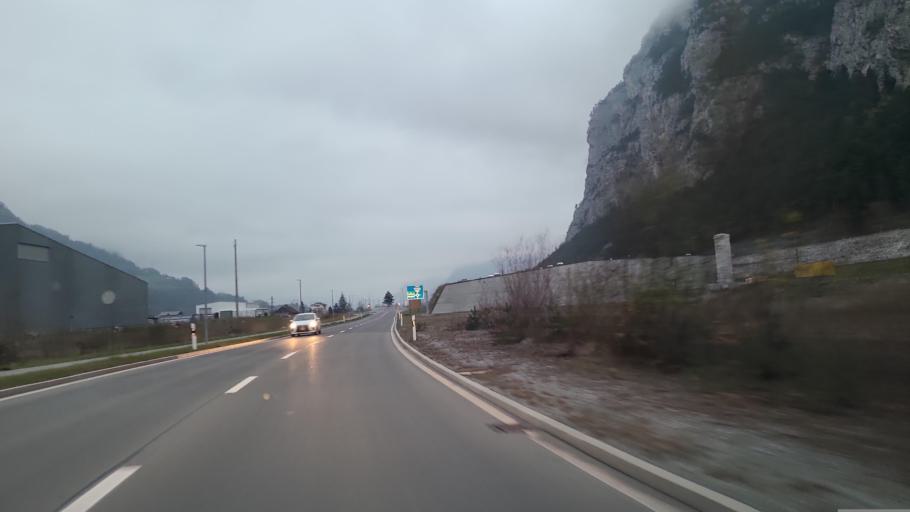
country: CH
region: Uri
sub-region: Uri
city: Erstfeld
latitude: 46.8326
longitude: 8.6459
